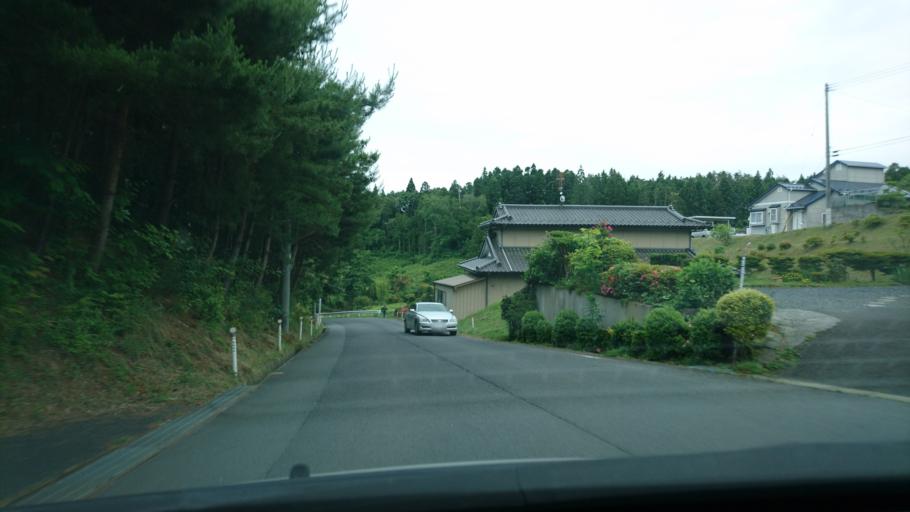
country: JP
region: Miyagi
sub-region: Oshika Gun
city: Onagawa Cho
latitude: 38.7781
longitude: 141.5129
